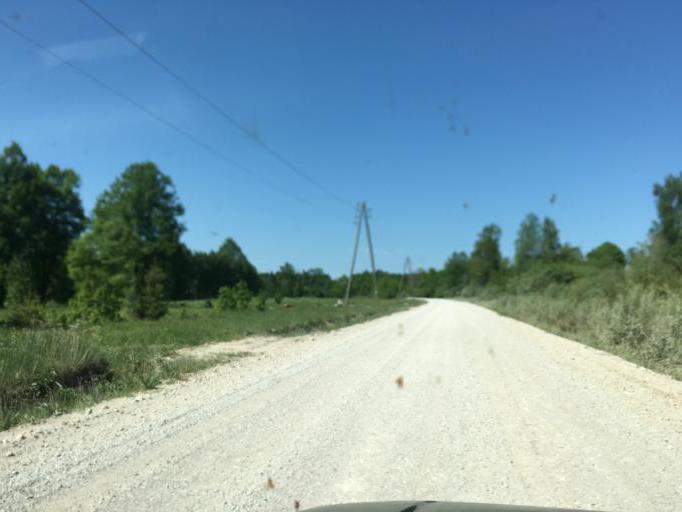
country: LV
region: Dundaga
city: Dundaga
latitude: 57.4473
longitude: 22.3212
